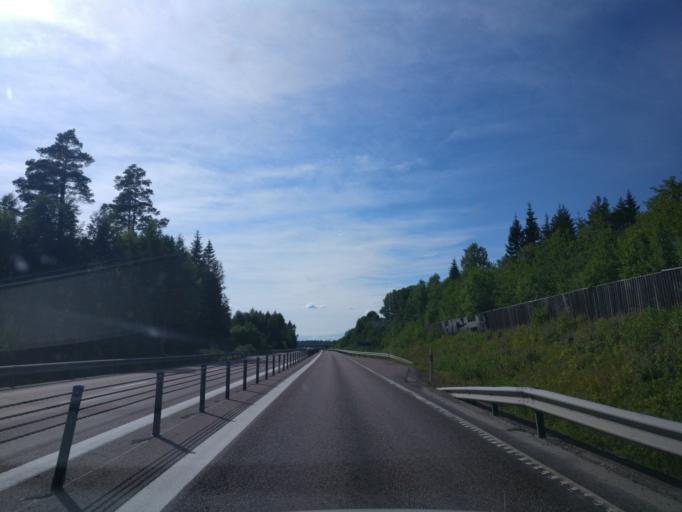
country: SE
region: Vaermland
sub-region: Kils Kommun
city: Kil
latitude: 59.4955
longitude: 13.3012
